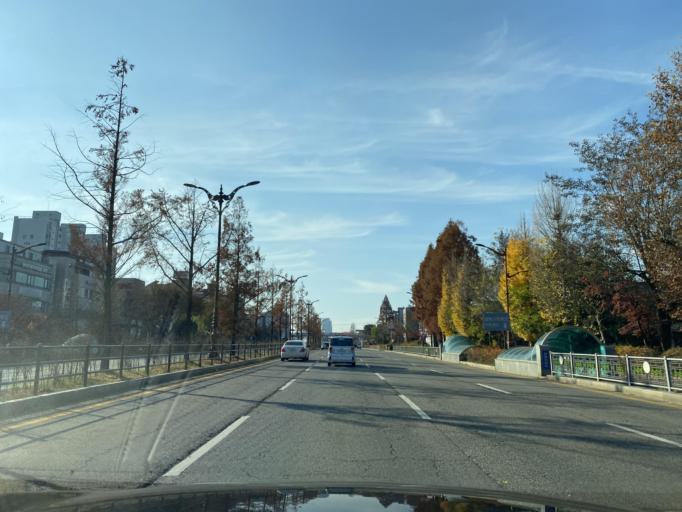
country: KR
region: Chungcheongnam-do
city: Cheonan
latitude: 36.7988
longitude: 127.1386
